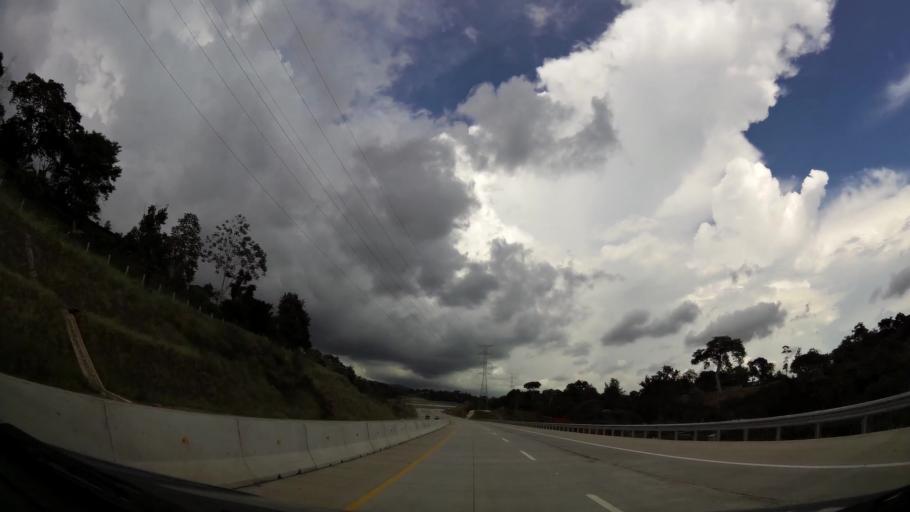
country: PA
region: Panama
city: Tocumen
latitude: 9.1057
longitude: -79.4101
